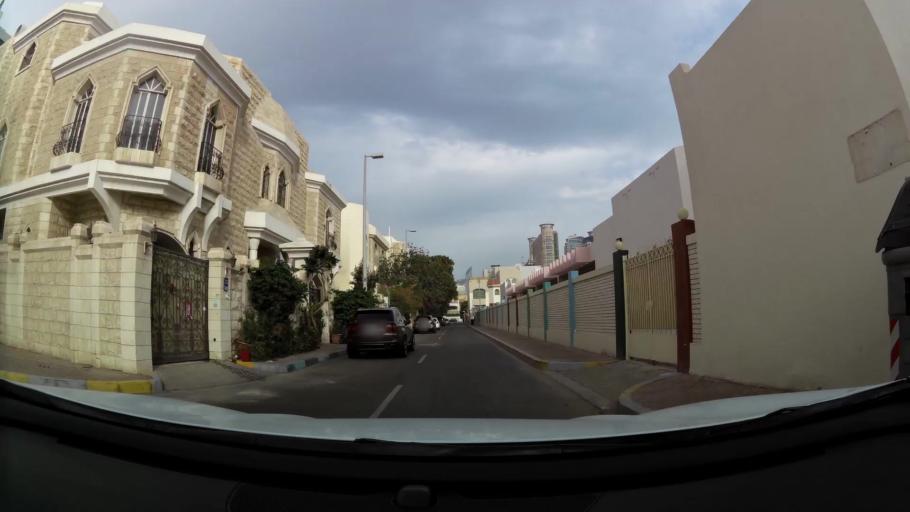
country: AE
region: Abu Dhabi
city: Abu Dhabi
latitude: 24.4653
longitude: 54.3775
